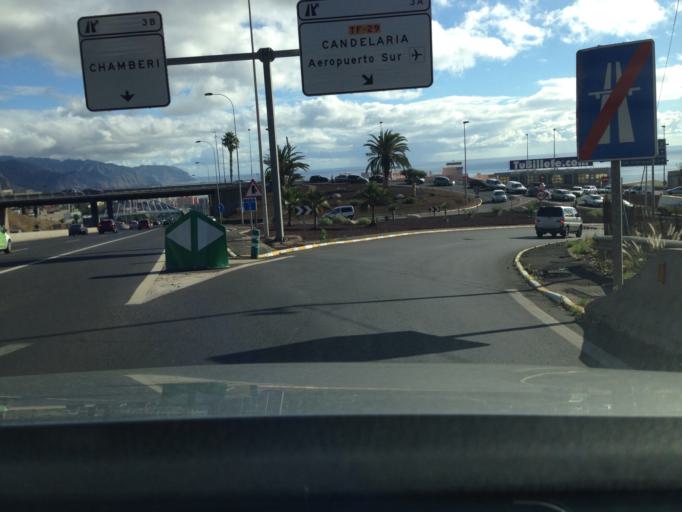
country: ES
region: Canary Islands
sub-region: Provincia de Santa Cruz de Tenerife
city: Santa Cruz de Tenerife
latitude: 28.4502
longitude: -16.2780
